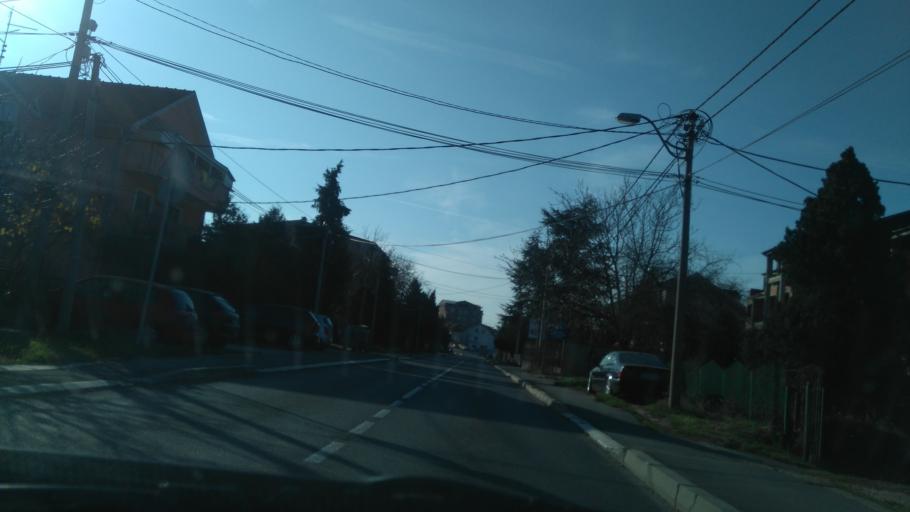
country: RS
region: Central Serbia
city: Sremcica
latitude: 44.7351
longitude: 20.3797
